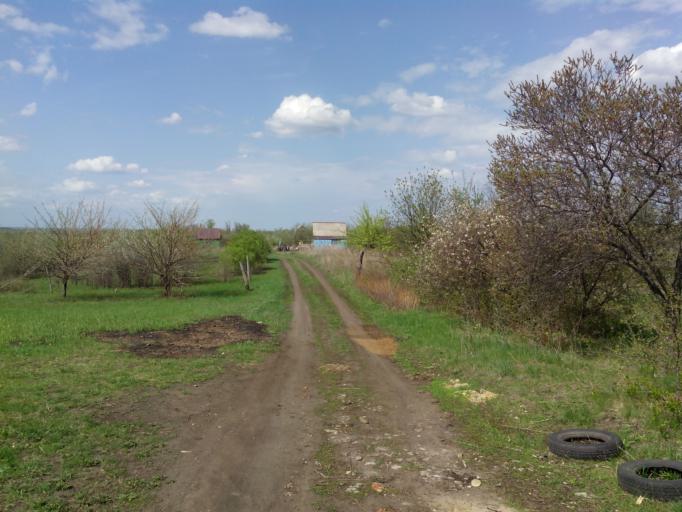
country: RU
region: Voronezj
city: Borisoglebsk
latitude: 51.3747
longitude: 42.1487
